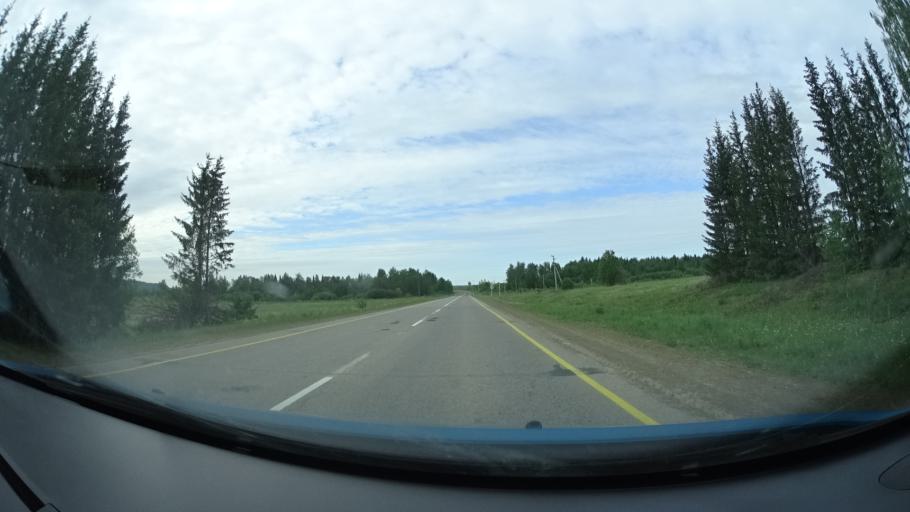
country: RU
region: Perm
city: Barda
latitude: 56.8699
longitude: 55.5963
